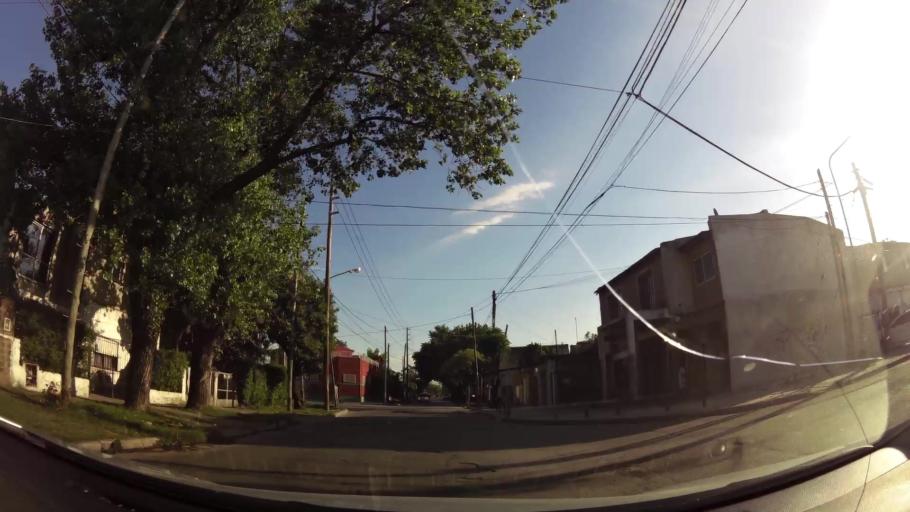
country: AR
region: Buenos Aires
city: Santa Catalina - Dique Lujan
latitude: -34.4623
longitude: -58.6646
